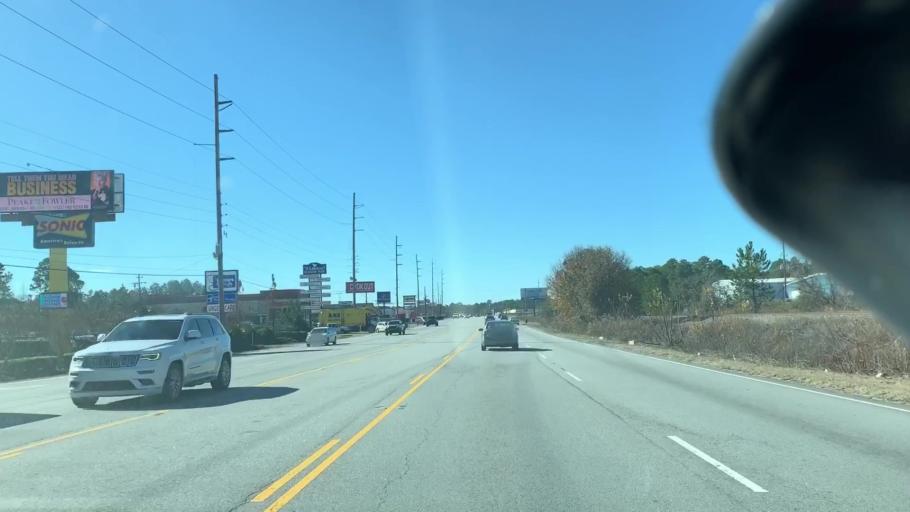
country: US
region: South Carolina
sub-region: Richland County
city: Woodfield
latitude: 34.1142
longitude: -80.8900
